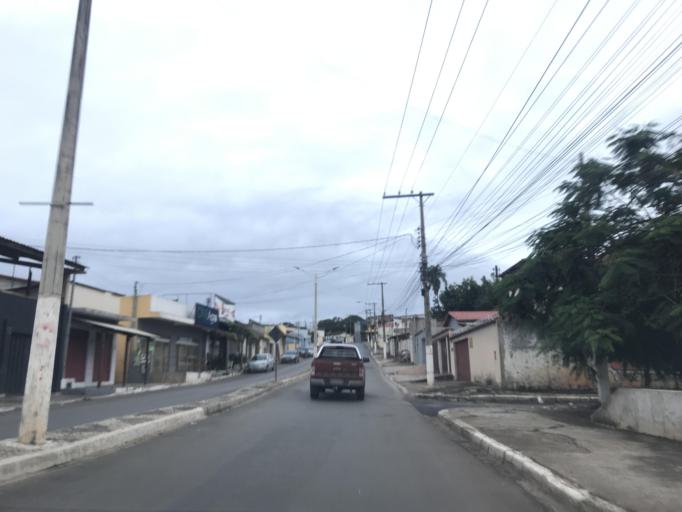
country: BR
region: Goias
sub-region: Luziania
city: Luziania
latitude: -16.2487
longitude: -47.9521
